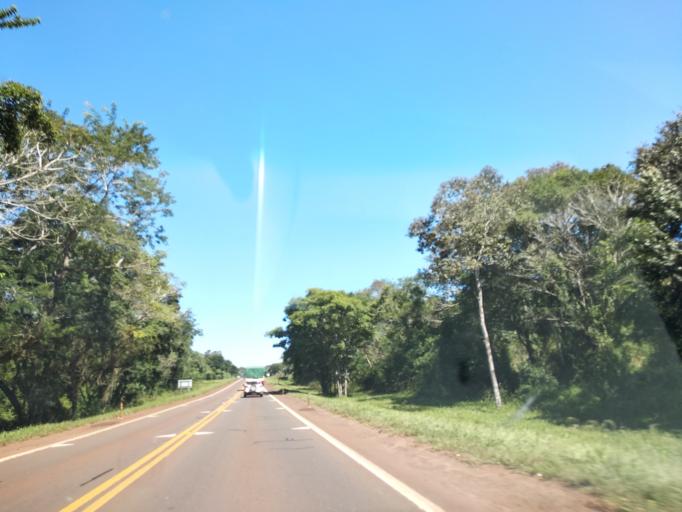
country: AR
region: Misiones
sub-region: Departamento de Iguazu
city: Puerto Iguazu
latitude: -25.7338
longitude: -54.5335
